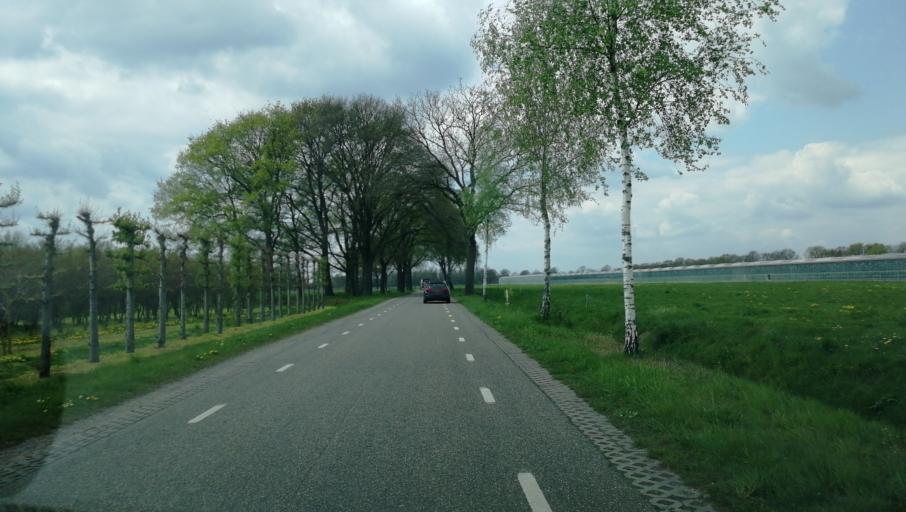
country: NL
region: Limburg
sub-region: Gemeente Peel en Maas
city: Maasbree
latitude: 51.4258
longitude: 6.0249
